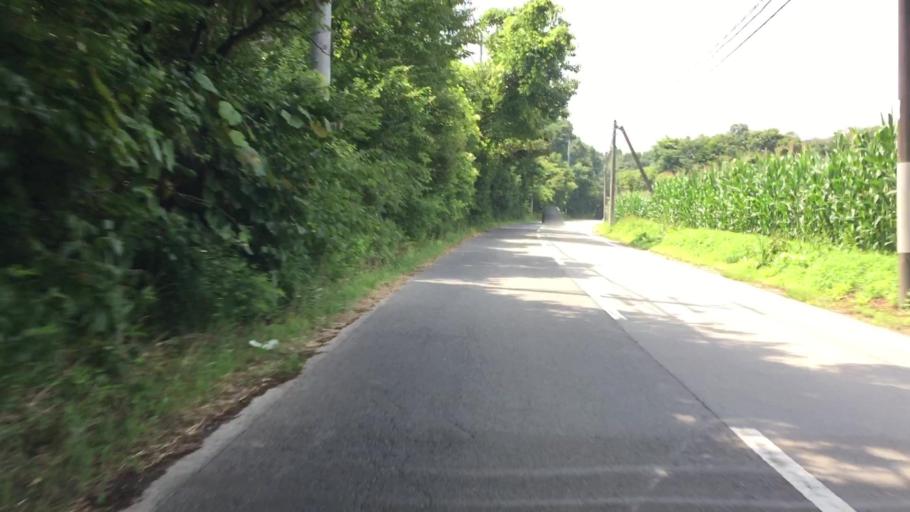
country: JP
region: Tochigi
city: Kuroiso
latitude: 36.9485
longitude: 139.9608
